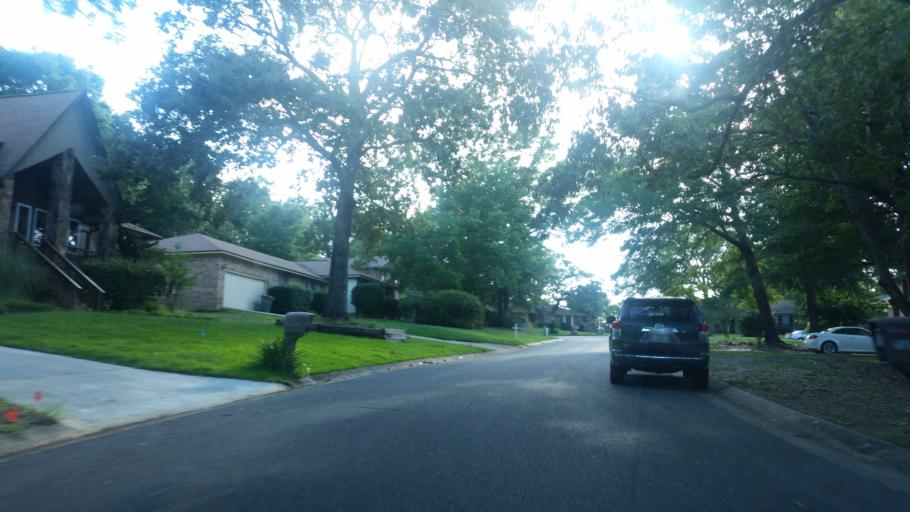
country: US
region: Florida
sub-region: Escambia County
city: Ferry Pass
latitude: 30.5086
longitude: -87.1677
